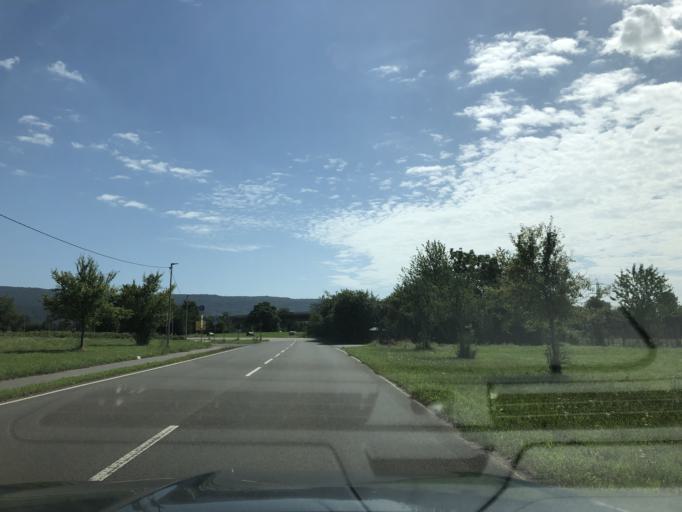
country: DE
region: Baden-Wuerttemberg
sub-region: Karlsruhe Region
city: Eppelheim
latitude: 49.3764
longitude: 8.6434
